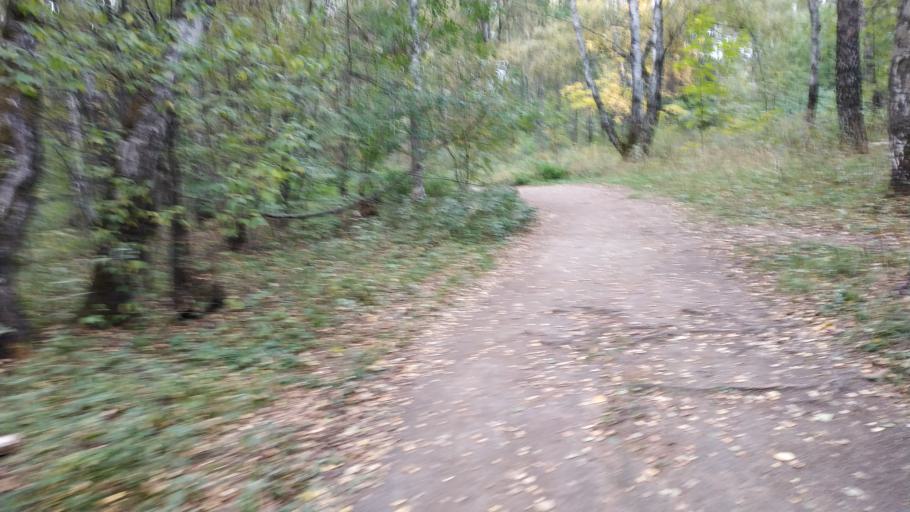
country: RU
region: Moscow
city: Khimki
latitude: 55.8680
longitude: 37.4312
